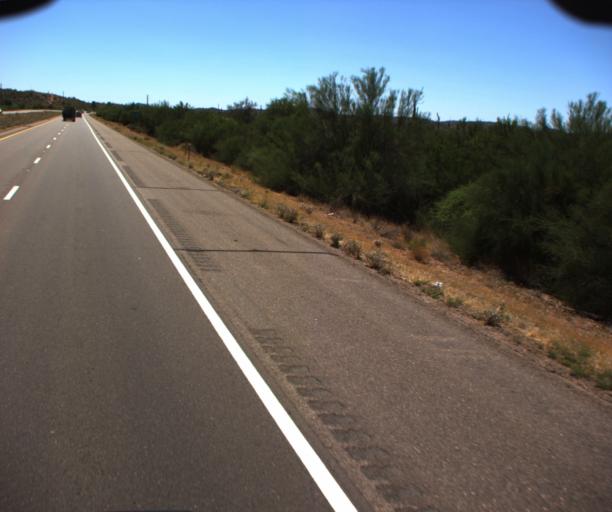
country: US
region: Arizona
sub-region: Maricopa County
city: Fountain Hills
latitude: 33.5711
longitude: -111.6996
